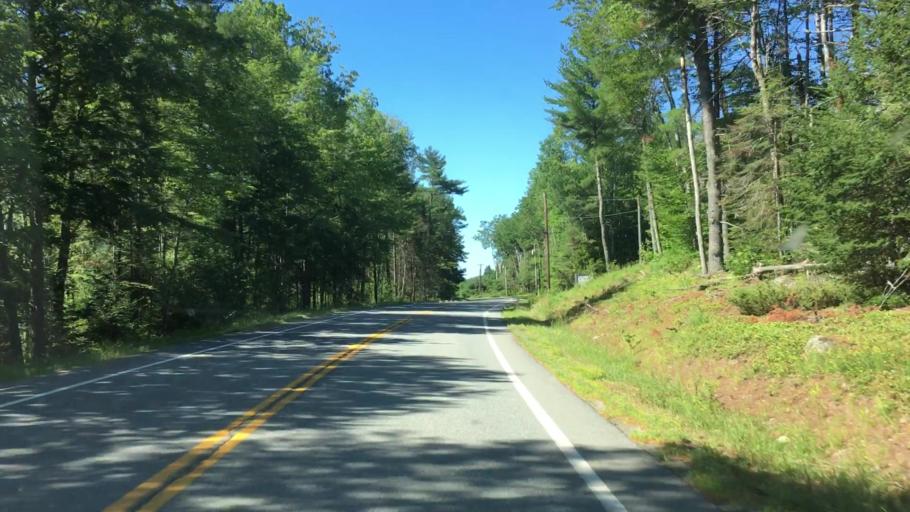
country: US
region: Maine
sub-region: Hancock County
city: Dedham
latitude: 44.6760
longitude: -68.6702
